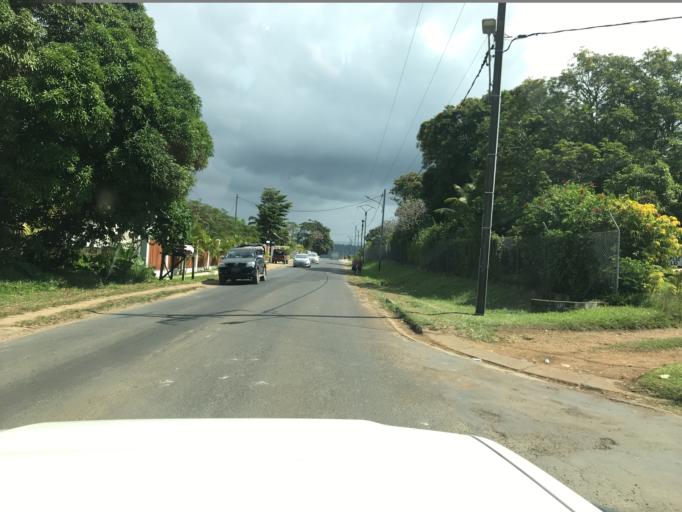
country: VU
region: Sanma
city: Luganville
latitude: -15.5104
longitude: 167.1844
